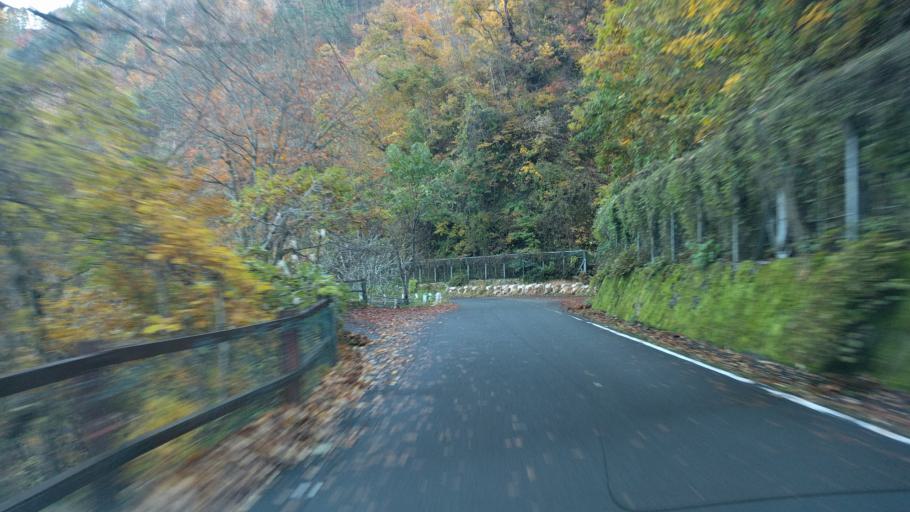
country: JP
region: Fukushima
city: Kitakata
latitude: 37.4593
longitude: 139.6206
